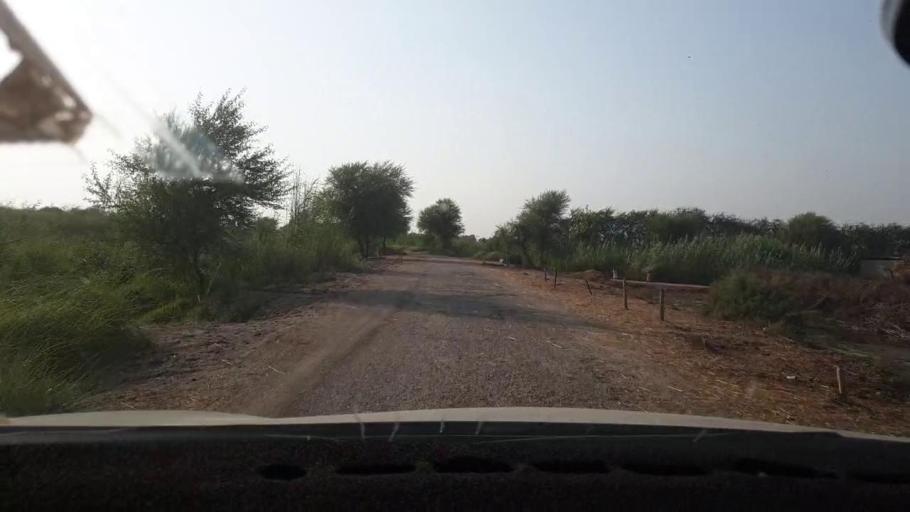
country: PK
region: Sindh
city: Berani
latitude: 25.8164
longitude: 68.7990
